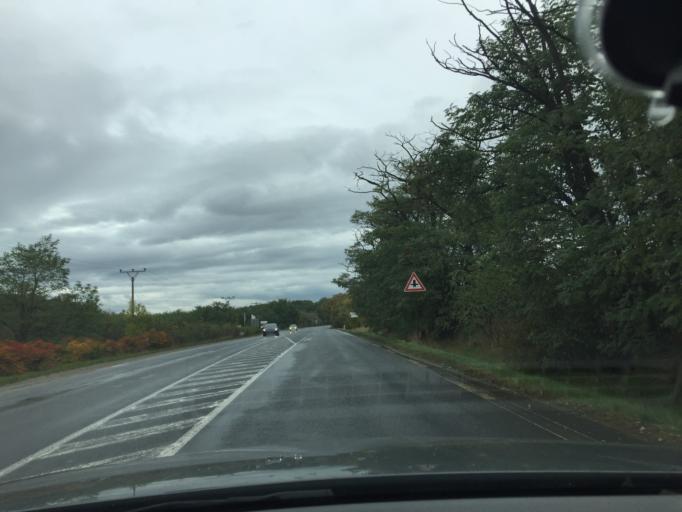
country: CZ
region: Central Bohemia
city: Velvary
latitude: 50.3437
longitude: 14.2760
